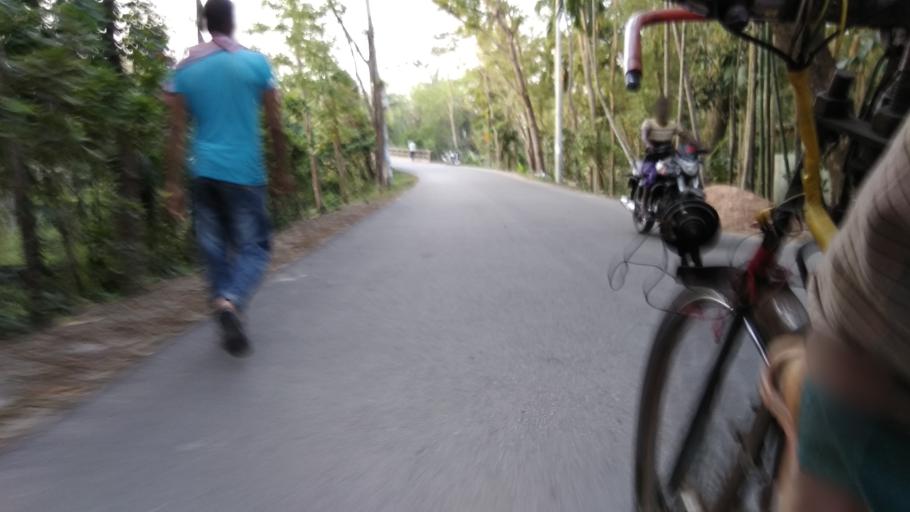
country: BD
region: Barisal
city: Mehendiganj
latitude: 22.9250
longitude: 90.4054
